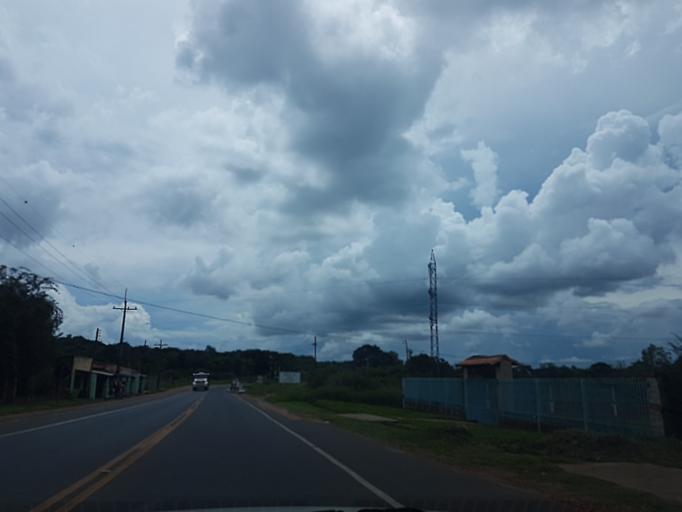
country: PY
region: Central
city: Limpio
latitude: -25.2369
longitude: -57.4382
